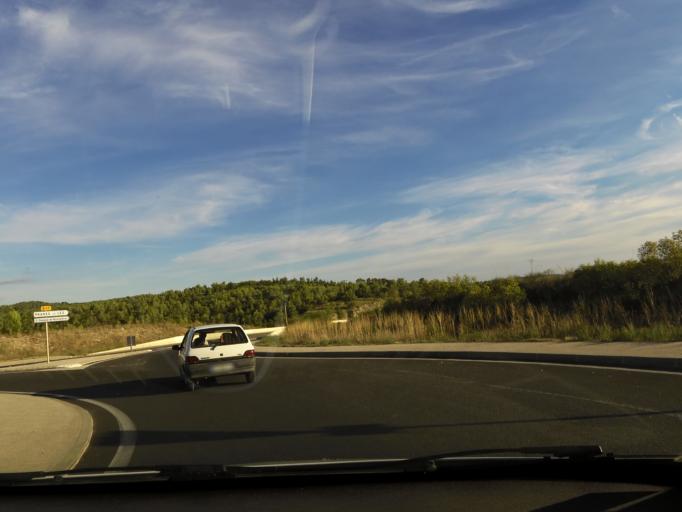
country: FR
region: Languedoc-Roussillon
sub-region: Departement de l'Herault
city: Prades-le-Lez
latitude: 43.7284
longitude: 3.8697
